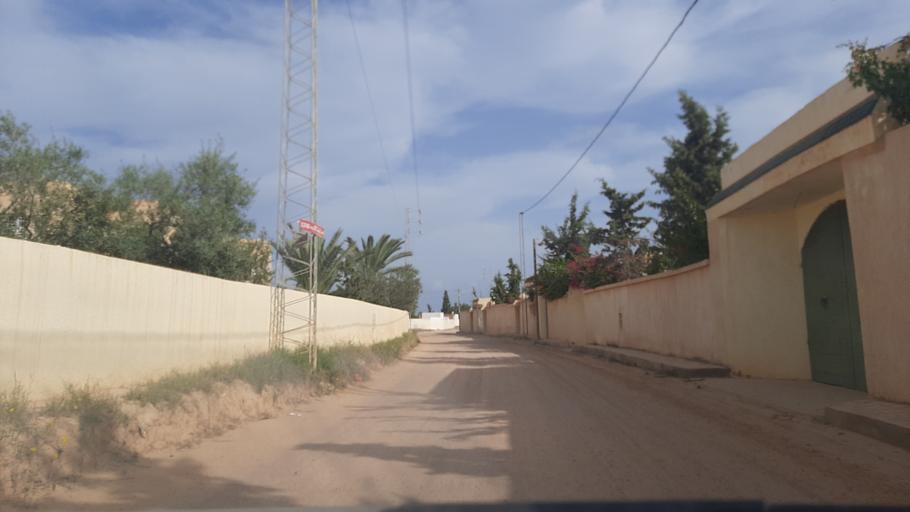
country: TN
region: Madanin
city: Midoun
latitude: 33.8155
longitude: 11.0251
